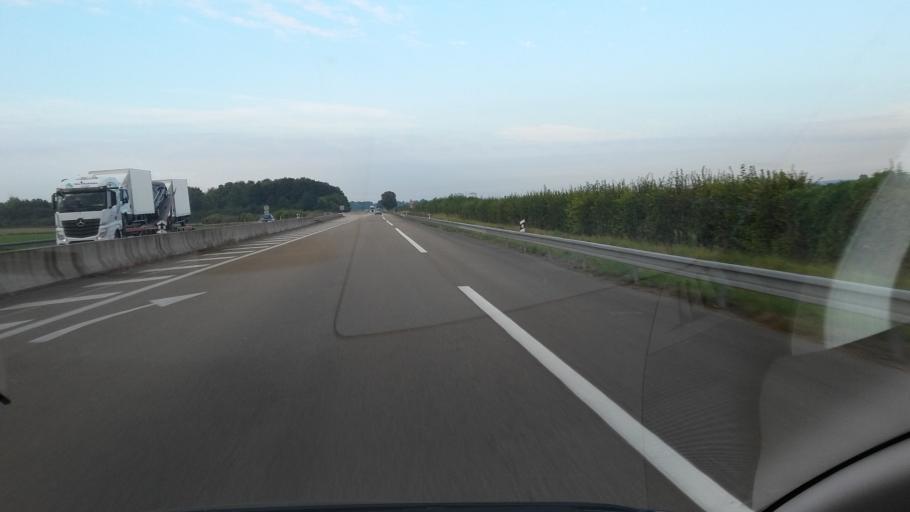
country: FR
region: Champagne-Ardenne
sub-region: Departement de la Marne
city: Connantre
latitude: 48.7422
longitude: 3.9564
